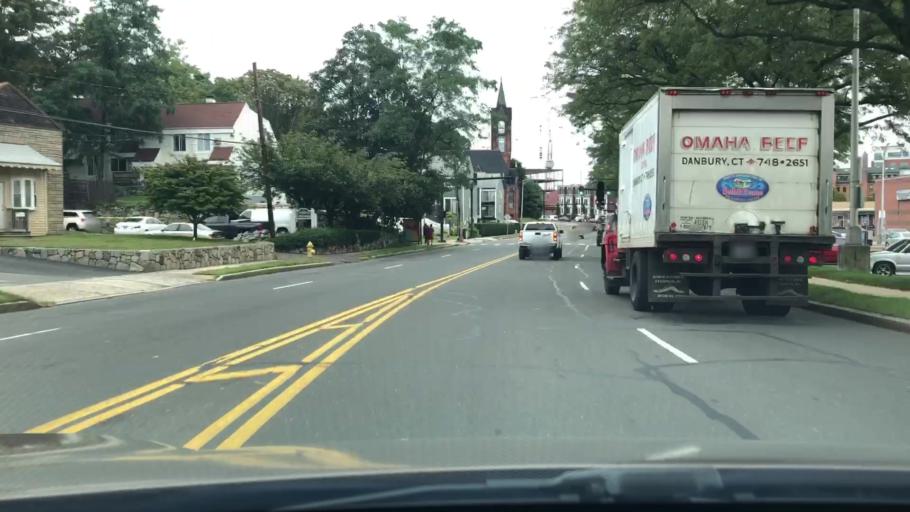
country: US
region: Connecticut
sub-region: Fairfield County
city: Norwalk
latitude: 41.1002
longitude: -73.4217
